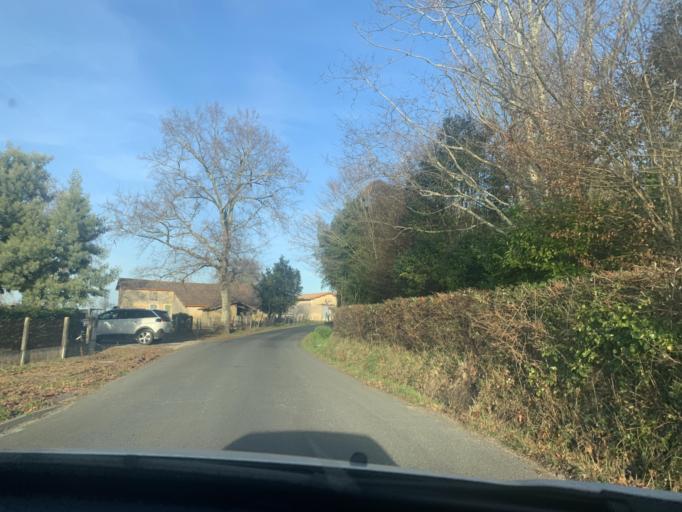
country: FR
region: Aquitaine
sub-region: Departement de la Gironde
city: Langon
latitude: 44.4932
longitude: -0.2619
